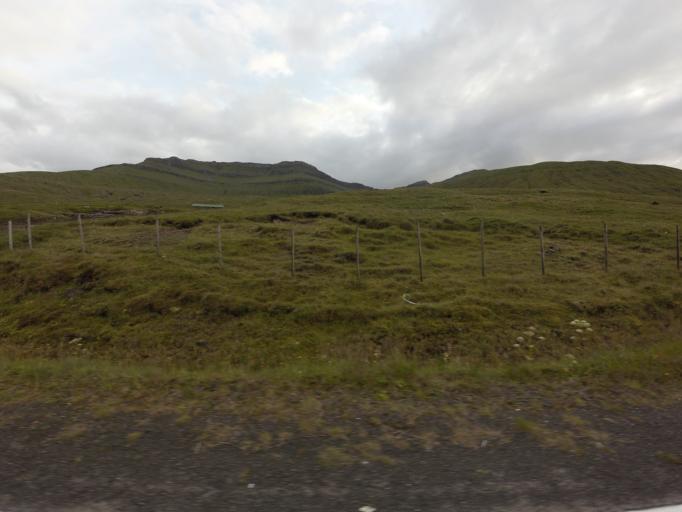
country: FO
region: Streymoy
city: Kollafjordhur
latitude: 62.1737
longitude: -6.9765
